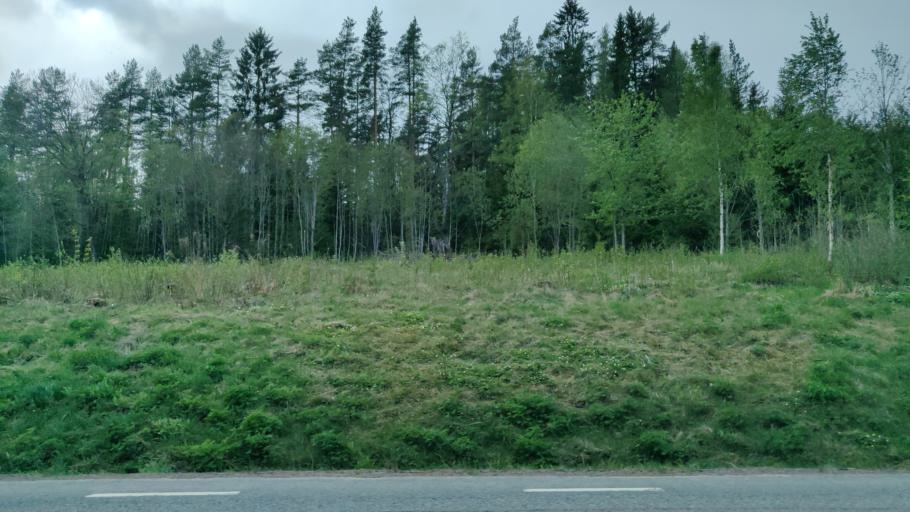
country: SE
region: Vaermland
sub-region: Forshaga Kommun
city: Deje
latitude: 59.6725
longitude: 13.4394
